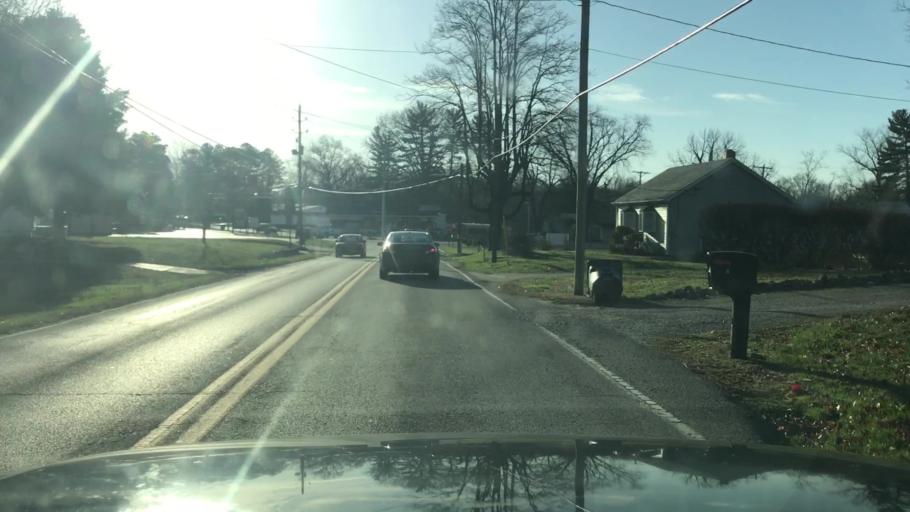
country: US
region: Indiana
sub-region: Vanderburgh County
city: Highland
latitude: 38.0343
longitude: -87.5633
